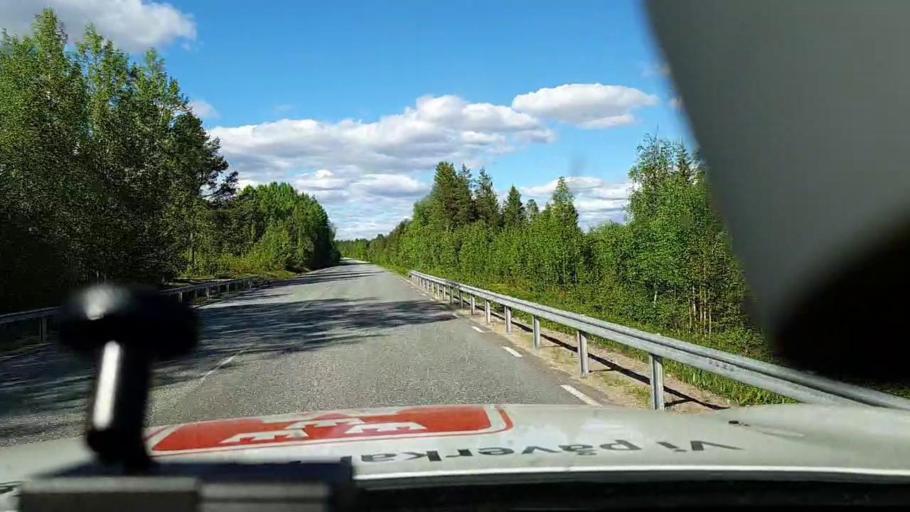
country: FI
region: Lapland
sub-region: Torniolaakso
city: Ylitornio
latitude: 66.3381
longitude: 23.6445
